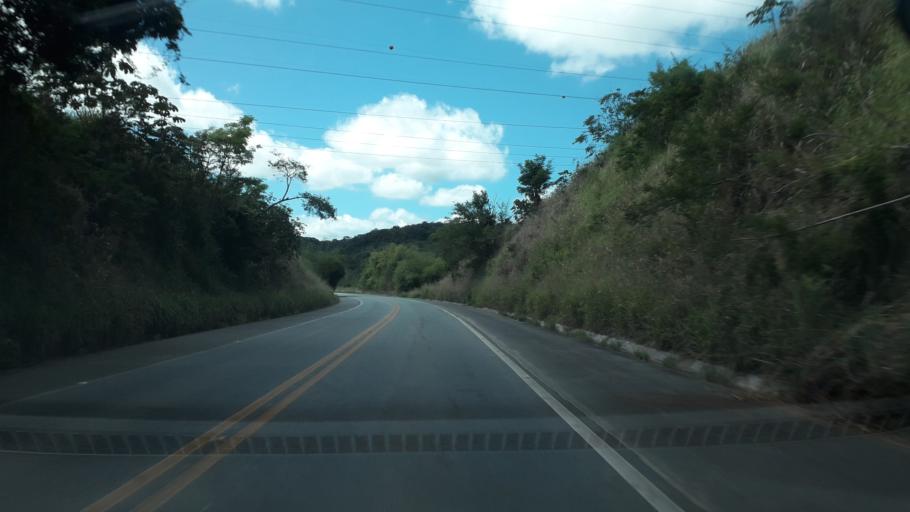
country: BR
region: Alagoas
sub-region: Messias
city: Messias
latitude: -9.3583
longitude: -35.8663
